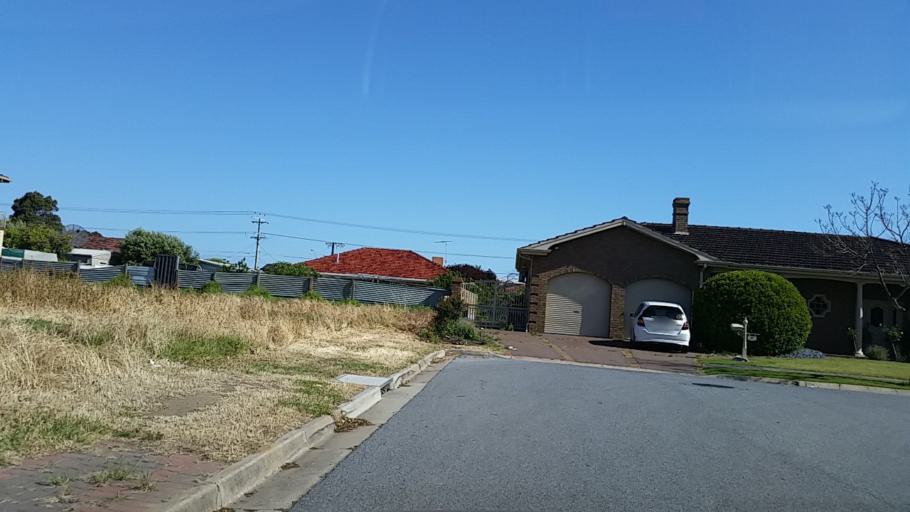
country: AU
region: South Australia
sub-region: Charles Sturt
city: Henley Beach
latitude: -34.9195
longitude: 138.5087
